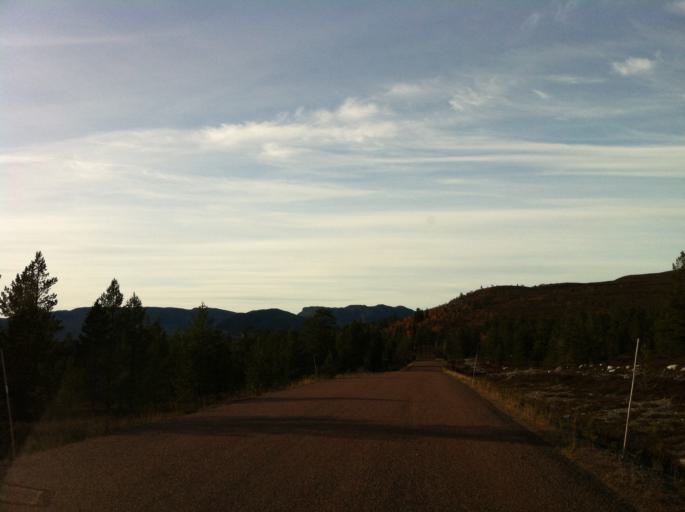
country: NO
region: Hedmark
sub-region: Engerdal
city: Engerdal
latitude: 62.0815
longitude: 12.1360
